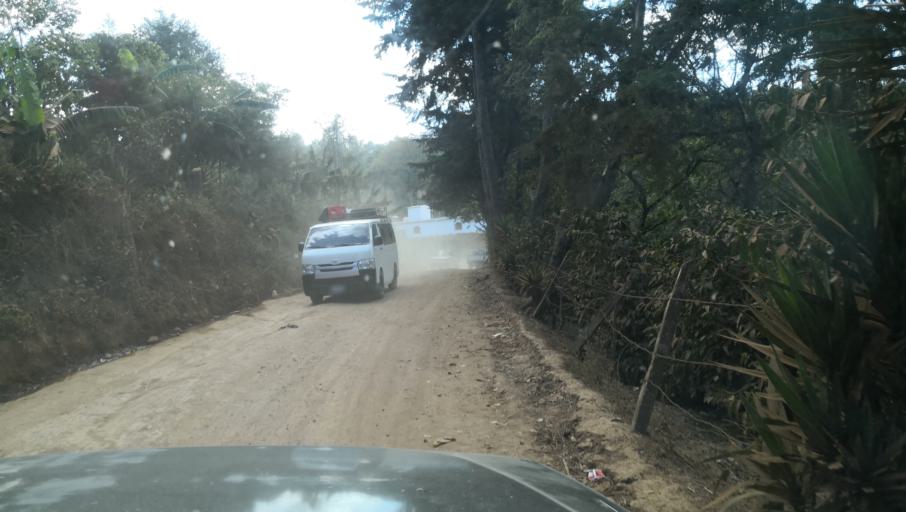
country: GT
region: Jalapa
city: San Carlos Alzatate
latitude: 14.3948
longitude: -89.9922
